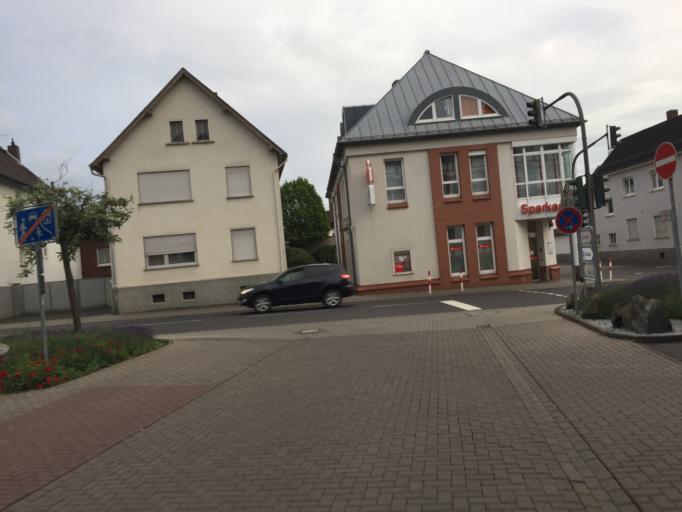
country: DE
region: Hesse
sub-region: Regierungsbezirk Giessen
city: Langgons
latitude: 50.5343
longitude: 8.7146
